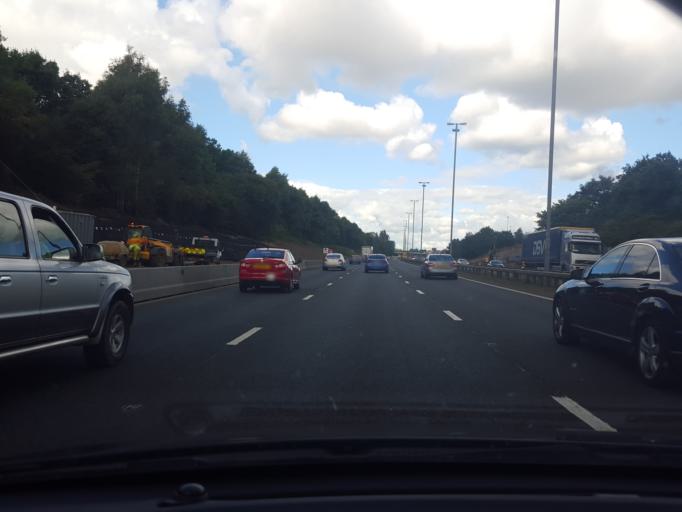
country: GB
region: Scotland
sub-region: South Lanarkshire
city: Bothwell
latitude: 55.8082
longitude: -4.0592
